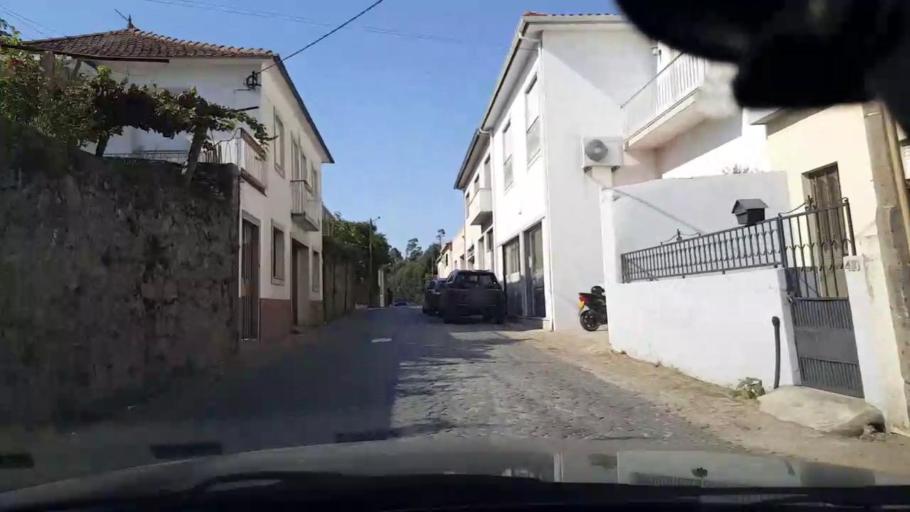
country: PT
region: Porto
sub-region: Vila do Conde
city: Arvore
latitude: 41.3822
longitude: -8.6832
